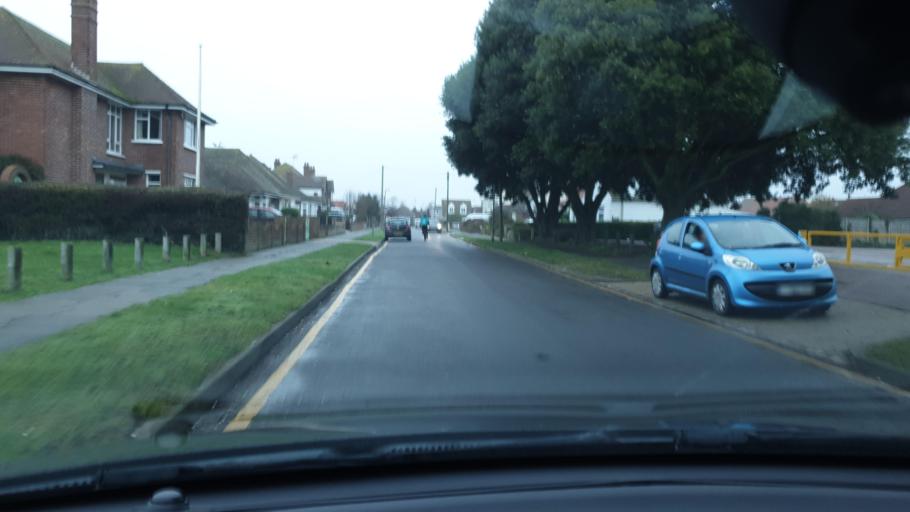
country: GB
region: England
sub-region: Essex
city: Clacton-on-Sea
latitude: 51.7972
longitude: 1.1800
